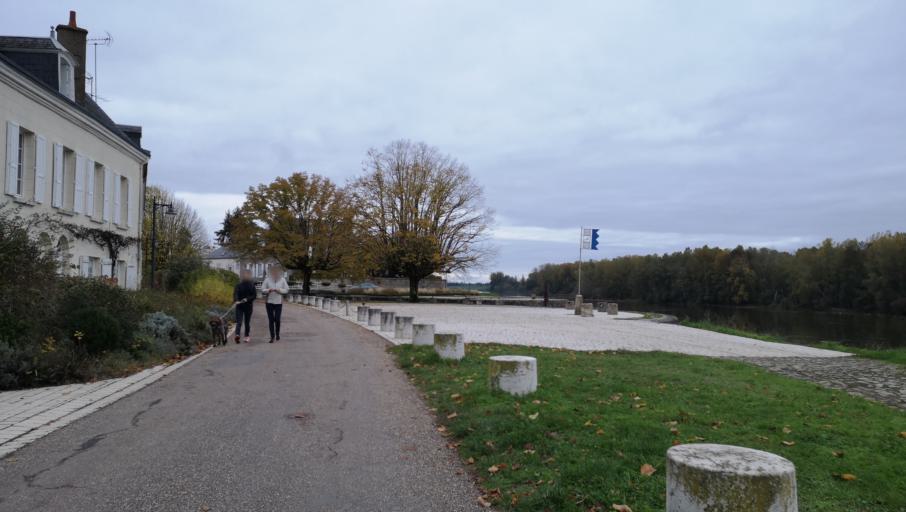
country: FR
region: Centre
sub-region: Departement du Loiret
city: Saint-Jean-de-Braye
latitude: 47.8994
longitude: 1.9845
